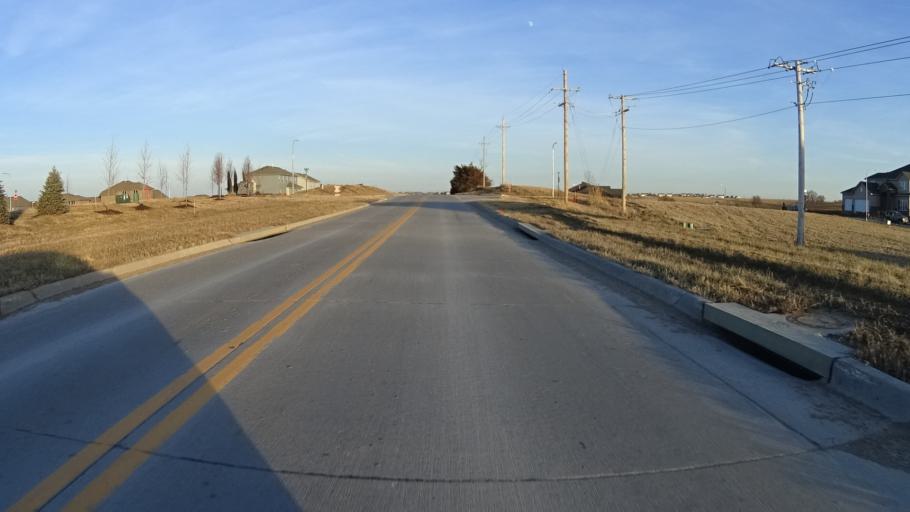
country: US
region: Nebraska
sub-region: Sarpy County
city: Papillion
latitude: 41.1326
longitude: -96.0876
